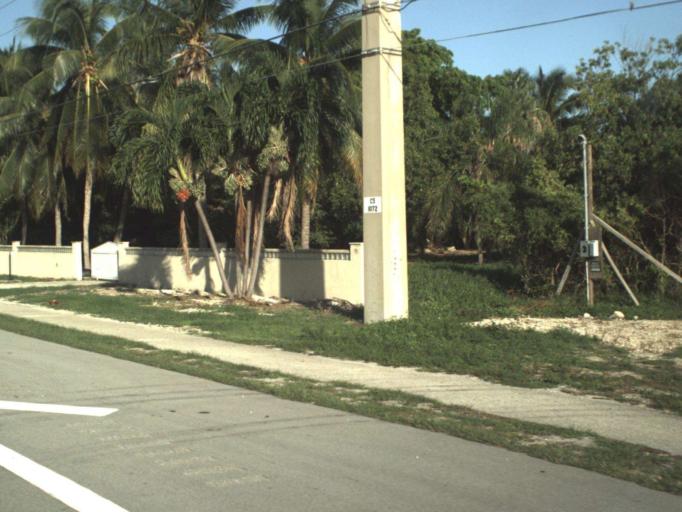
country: US
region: Florida
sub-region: Monroe County
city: Islamorada
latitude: 24.8047
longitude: -80.8460
